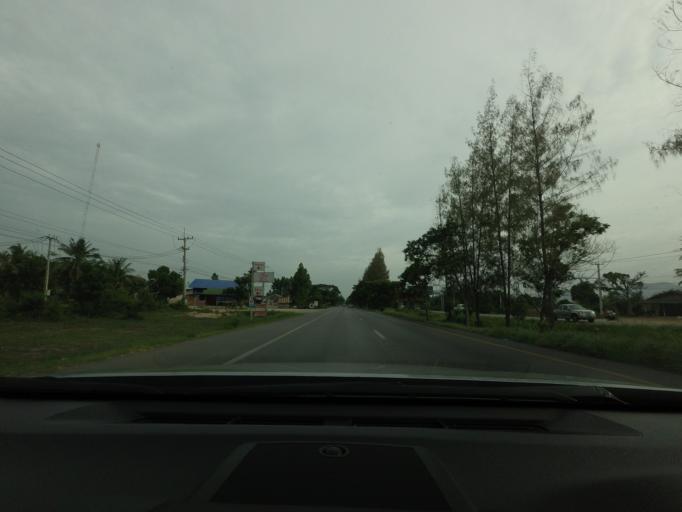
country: TH
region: Phetchaburi
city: Cha-am
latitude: 12.7986
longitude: 99.9415
